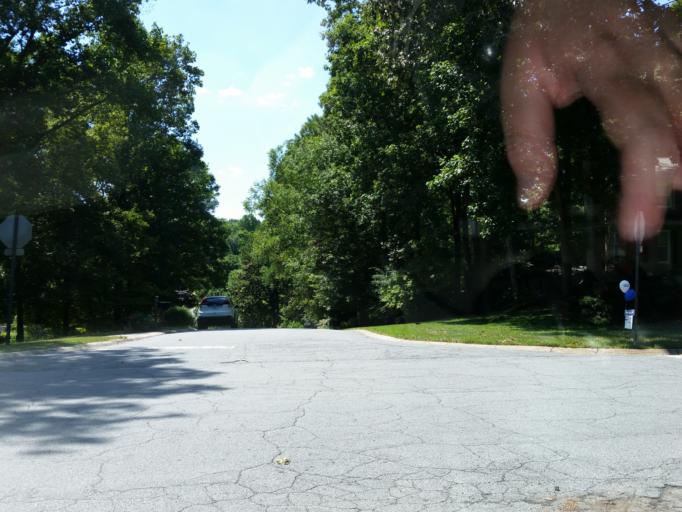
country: US
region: Georgia
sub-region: Cobb County
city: Marietta
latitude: 33.9543
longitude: -84.4849
